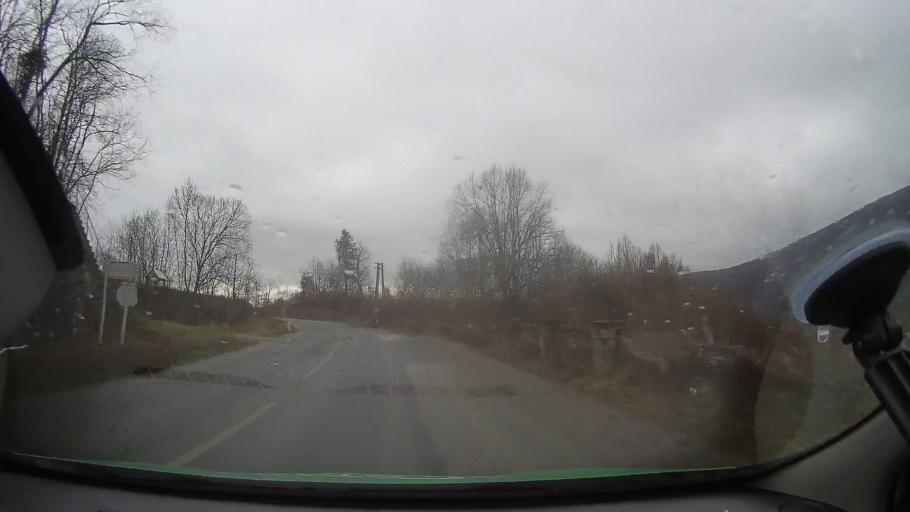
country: RO
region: Arad
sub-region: Comuna Halmagiu
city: Halmagiu
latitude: 46.2352
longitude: 22.5576
